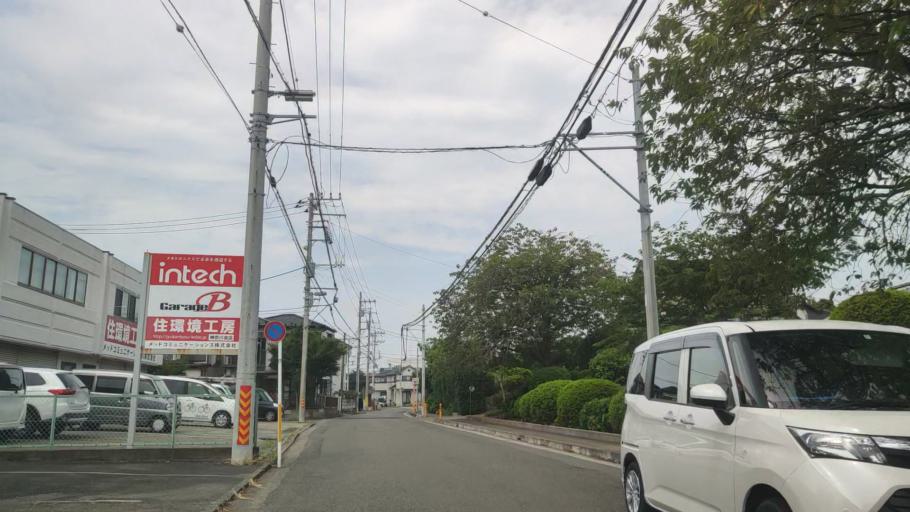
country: JP
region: Kanagawa
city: Atsugi
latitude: 35.4223
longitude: 139.3967
